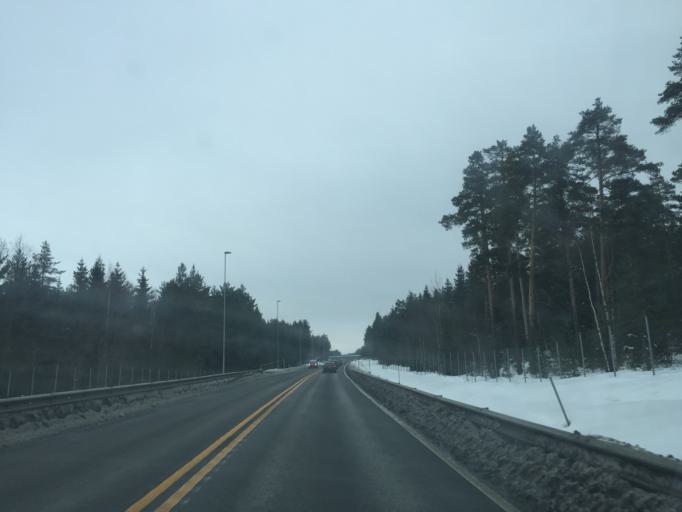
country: NO
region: Hedmark
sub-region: Loten
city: Loten
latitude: 60.7519
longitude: 11.3019
